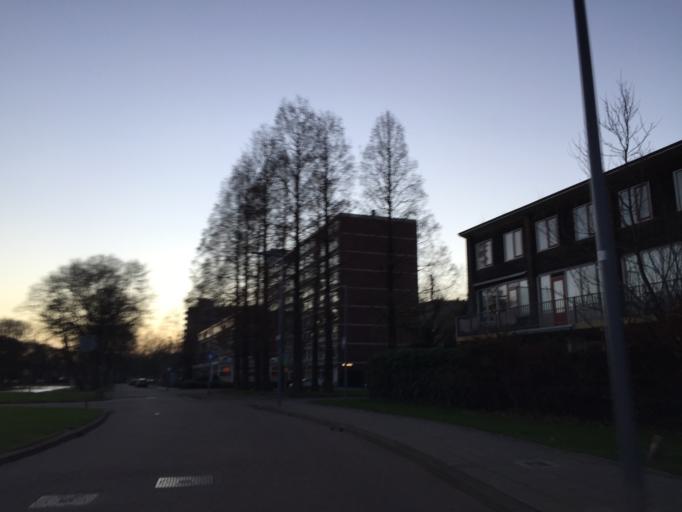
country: NL
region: South Holland
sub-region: Gemeente Rotterdam
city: Rotterdam
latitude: 51.9567
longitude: 4.4718
